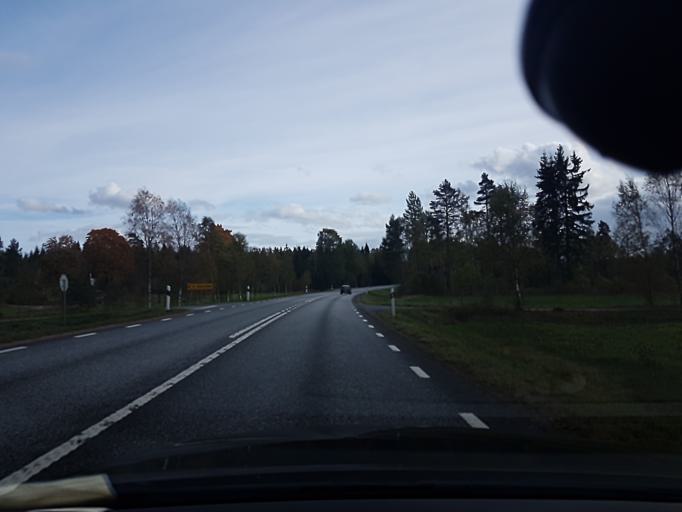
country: SE
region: Joenkoeping
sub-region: Varnamo Kommun
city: Bredaryd
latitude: 57.1771
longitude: 13.7595
